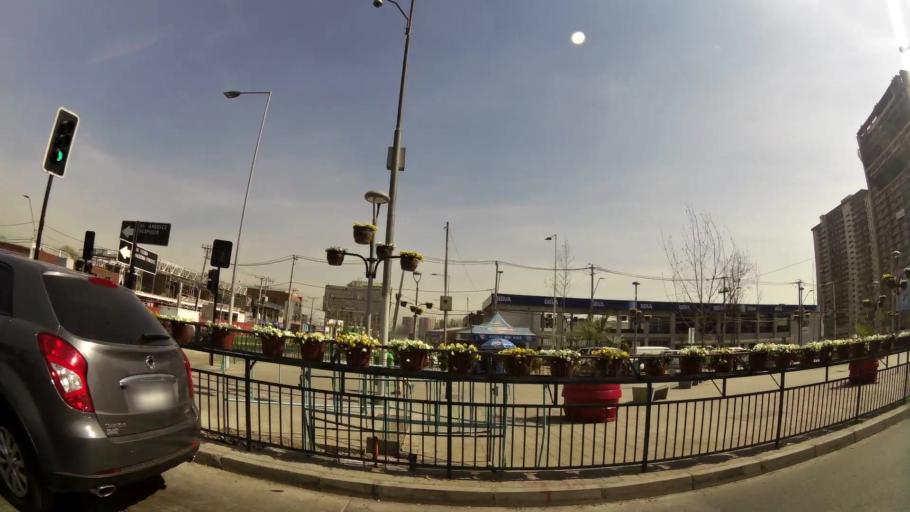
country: CL
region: Santiago Metropolitan
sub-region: Provincia de Santiago
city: Villa Presidente Frei, Nunoa, Santiago, Chile
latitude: -33.5226
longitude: -70.5988
